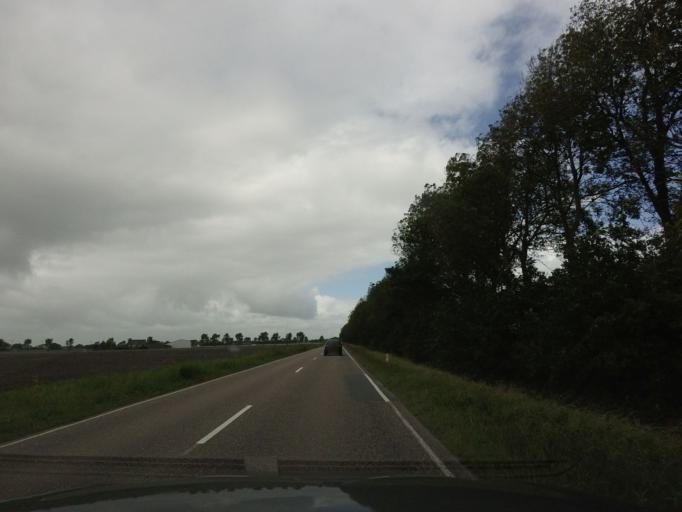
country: NL
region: North Holland
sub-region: Gemeente Langedijk
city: Broek op Langedijk
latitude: 52.6924
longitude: 4.8024
